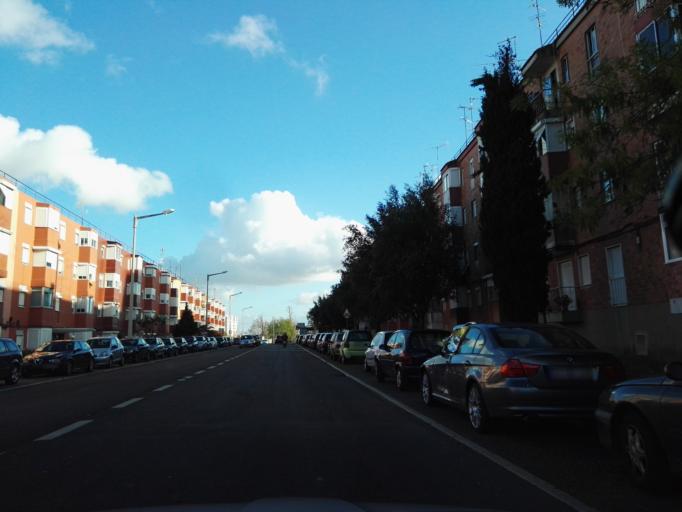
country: PT
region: Lisbon
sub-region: Loures
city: Moscavide
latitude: 38.7725
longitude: -9.1103
